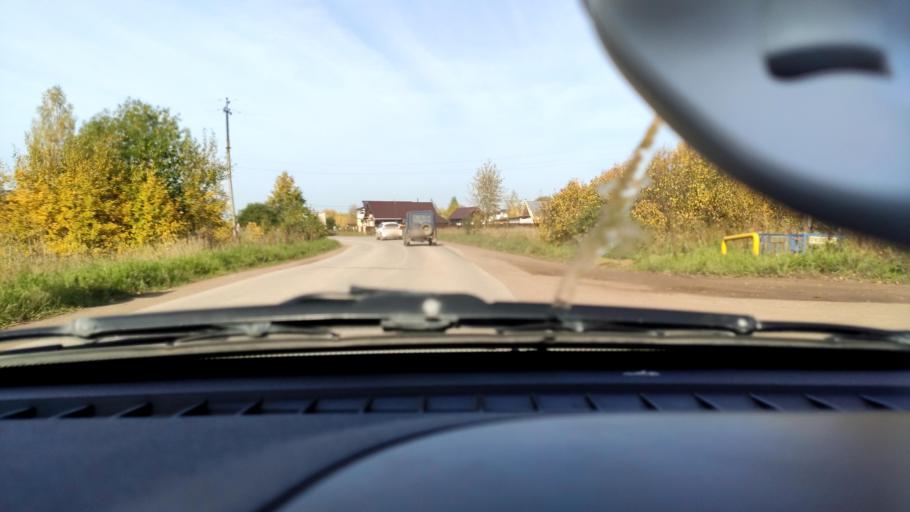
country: RU
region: Perm
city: Overyata
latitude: 58.0846
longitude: 55.8773
